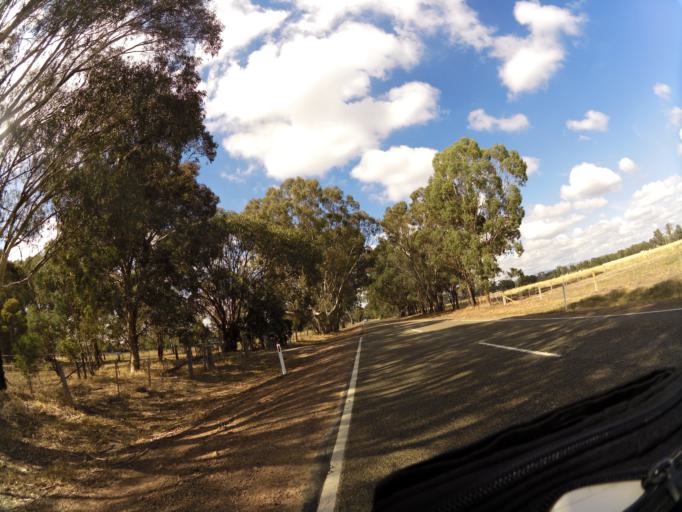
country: AU
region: Victoria
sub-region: Benalla
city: Benalla
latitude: -36.5884
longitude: 146.0093
